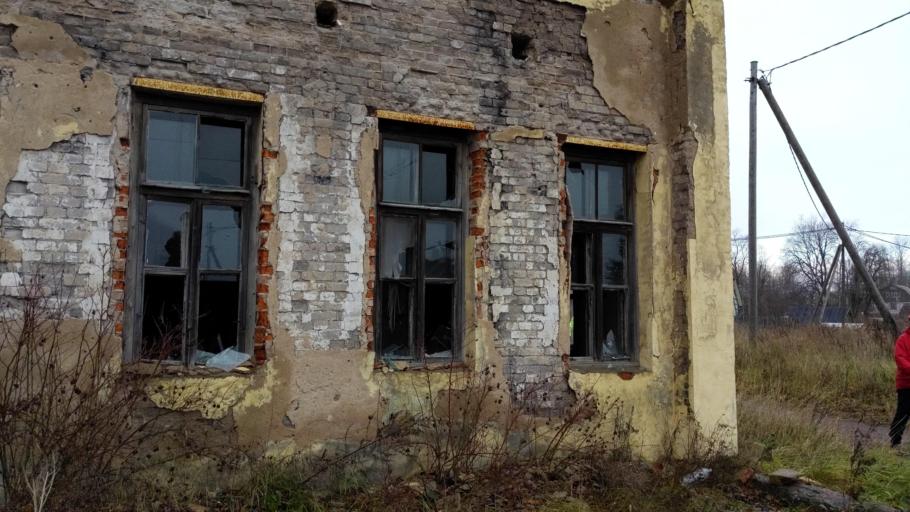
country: RU
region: Leningrad
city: Vysotsk
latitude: 60.7753
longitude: 28.5544
